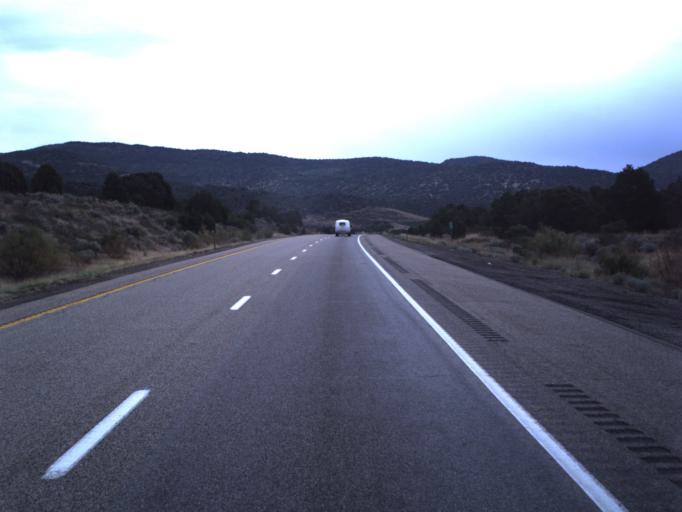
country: US
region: Utah
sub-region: Beaver County
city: Beaver
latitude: 38.6064
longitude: -112.5251
